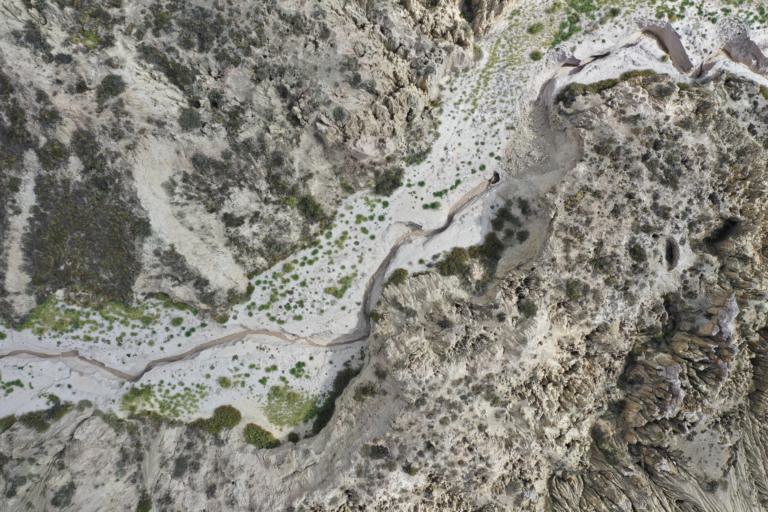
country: BO
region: La Paz
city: La Paz
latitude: -16.5637
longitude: -68.1210
